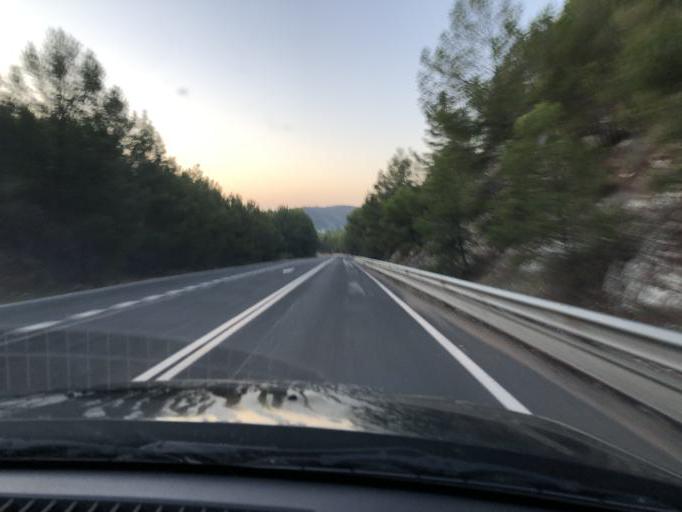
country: ES
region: Balearic Islands
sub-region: Illes Balears
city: Andratx
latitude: 39.5572
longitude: 2.4197
